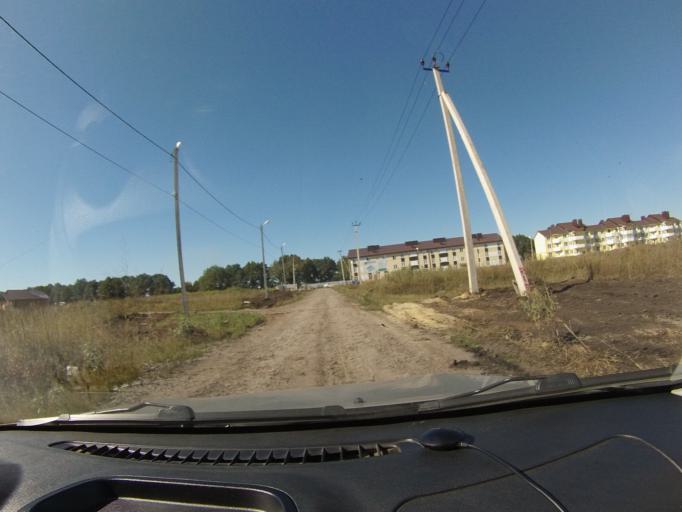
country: RU
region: Tambov
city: Komsomolets
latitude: 52.7827
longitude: 41.3670
